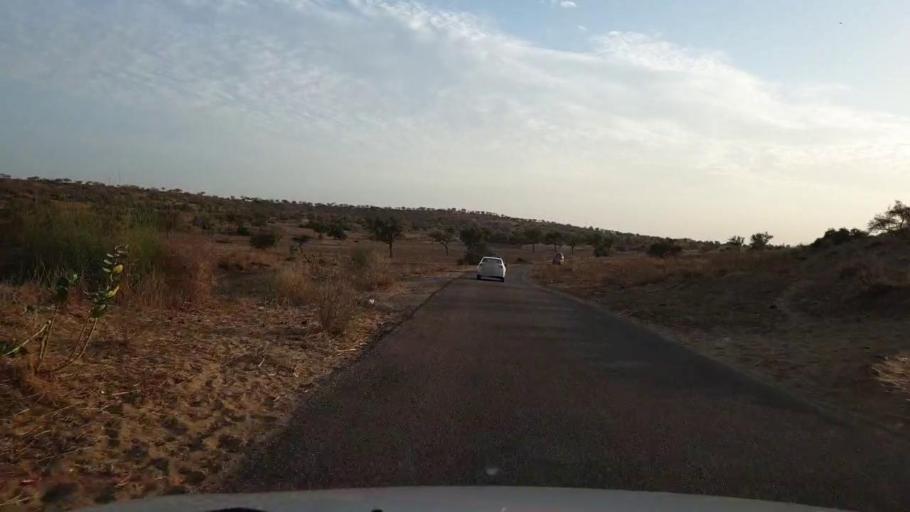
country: PK
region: Sindh
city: Nabisar
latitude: 25.0311
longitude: 69.9498
